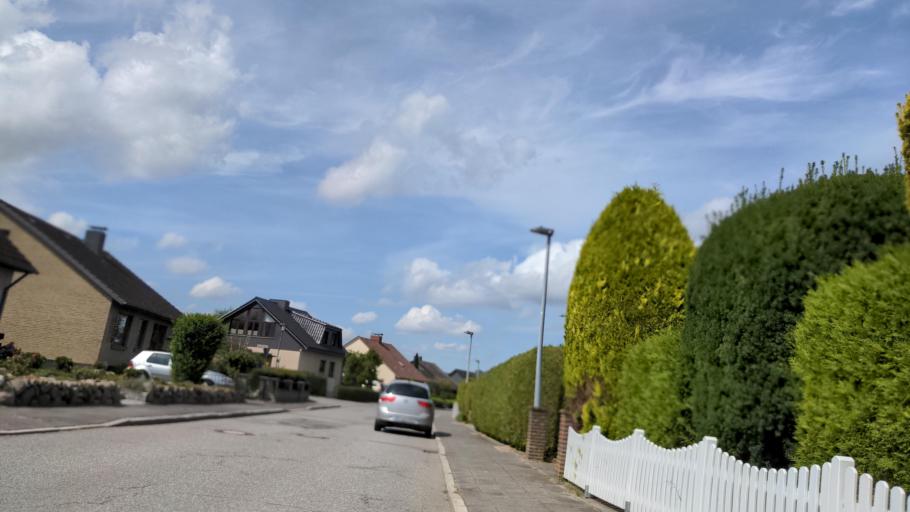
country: DE
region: Schleswig-Holstein
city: Eutin
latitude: 54.1234
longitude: 10.6069
